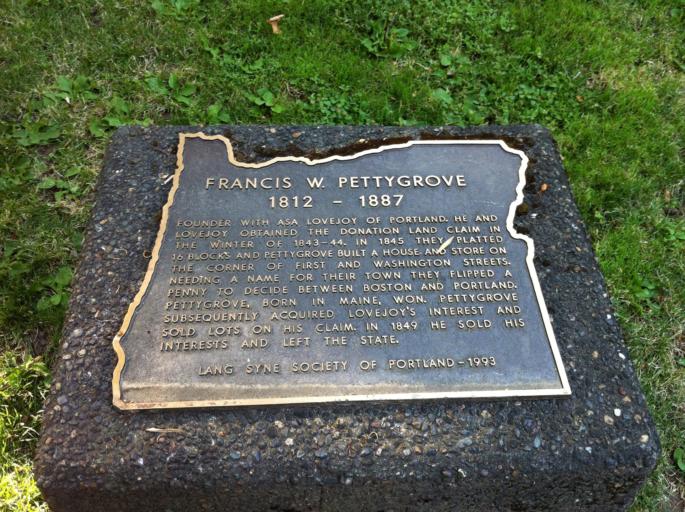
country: US
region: Oregon
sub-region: Multnomah County
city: Portland
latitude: 45.5109
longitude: -122.6787
